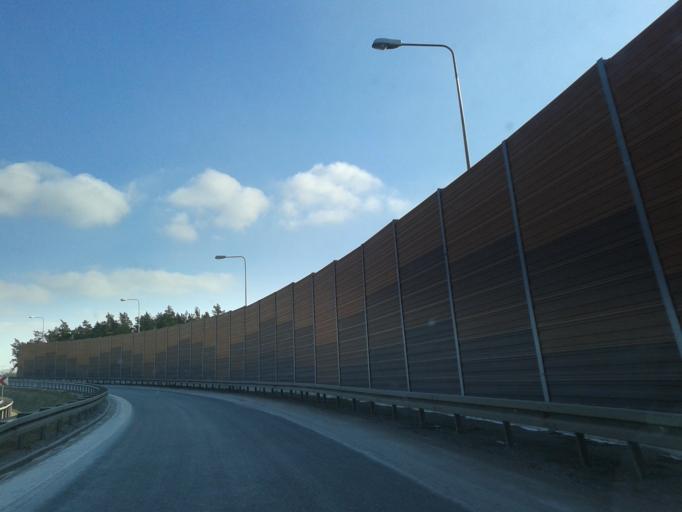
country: PL
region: Kujawsko-Pomorskie
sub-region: Powiat aleksandrowski
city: Ciechocinek
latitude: 52.8660
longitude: 18.7569
